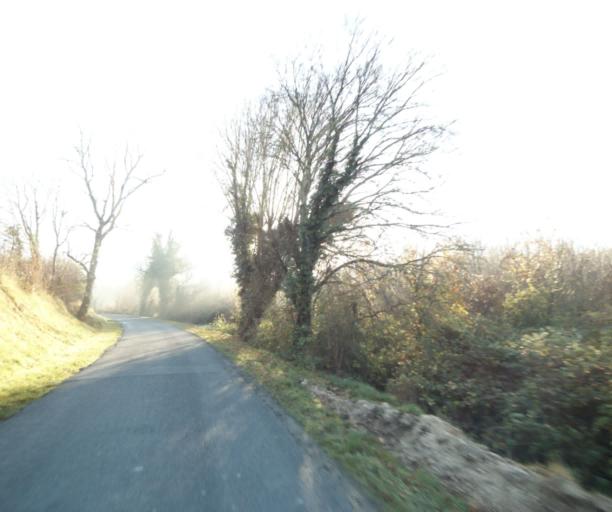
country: FR
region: Poitou-Charentes
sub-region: Departement de la Charente-Maritime
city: Cherac
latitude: 45.7034
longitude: -0.4295
